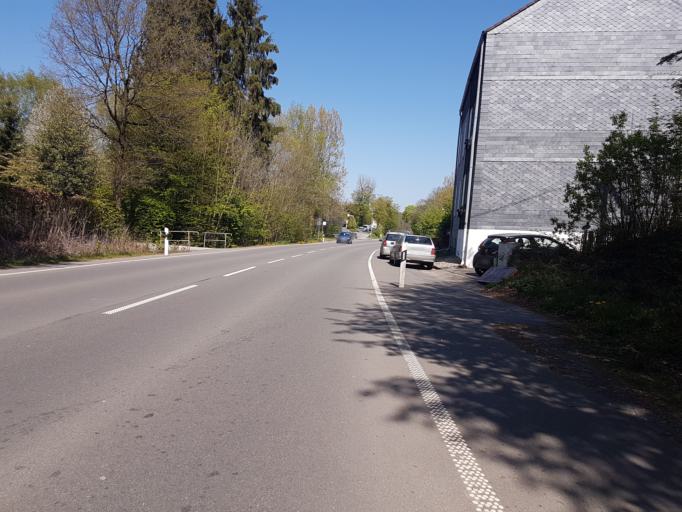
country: DE
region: North Rhine-Westphalia
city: Gevelsberg
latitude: 51.3590
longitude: 7.3297
